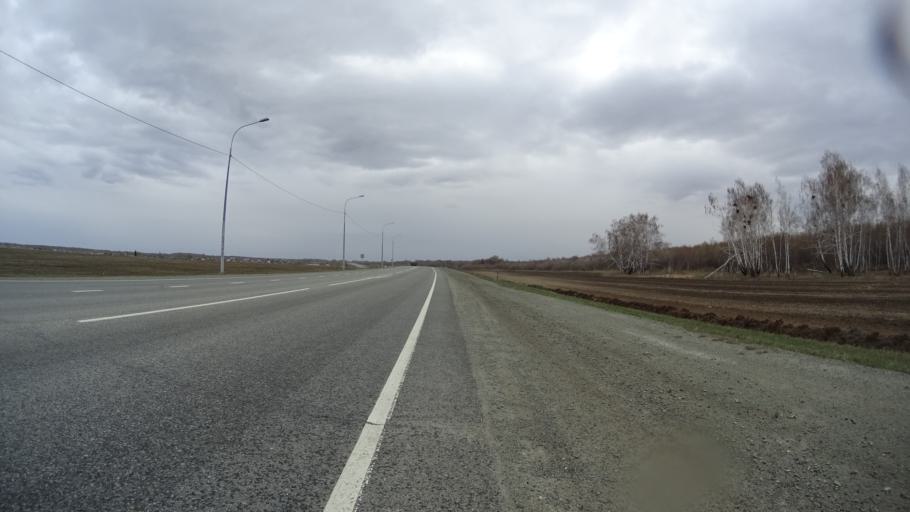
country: RU
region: Chelyabinsk
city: Krasnogorskiy
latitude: 54.6820
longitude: 61.2470
